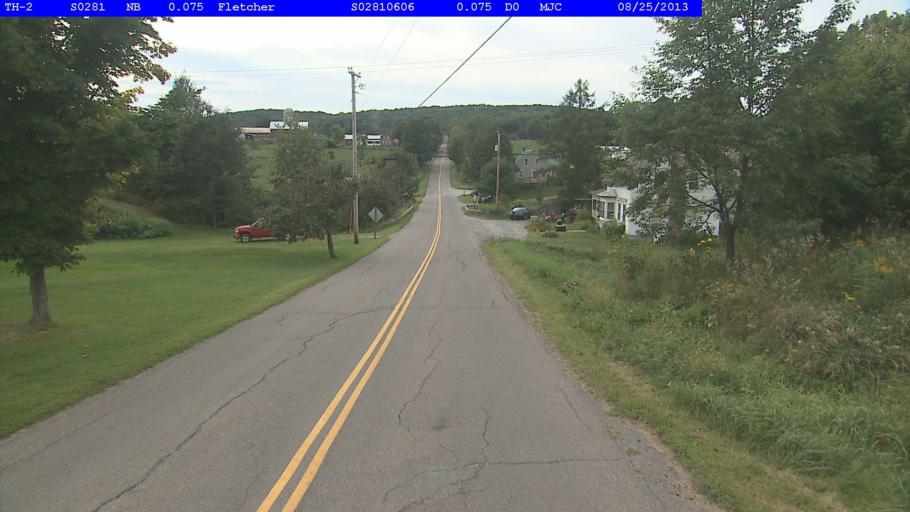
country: US
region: Vermont
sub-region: Chittenden County
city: Jericho
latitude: 44.6838
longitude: -72.9157
